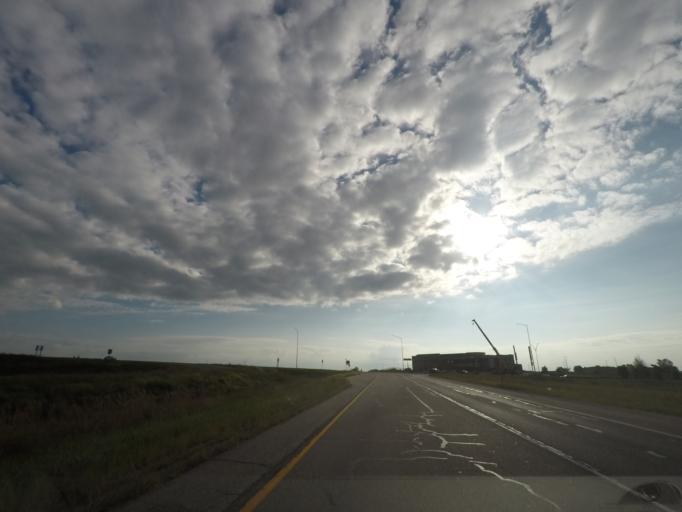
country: US
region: Iowa
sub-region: Polk County
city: Altoona
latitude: 41.6657
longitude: -93.4661
